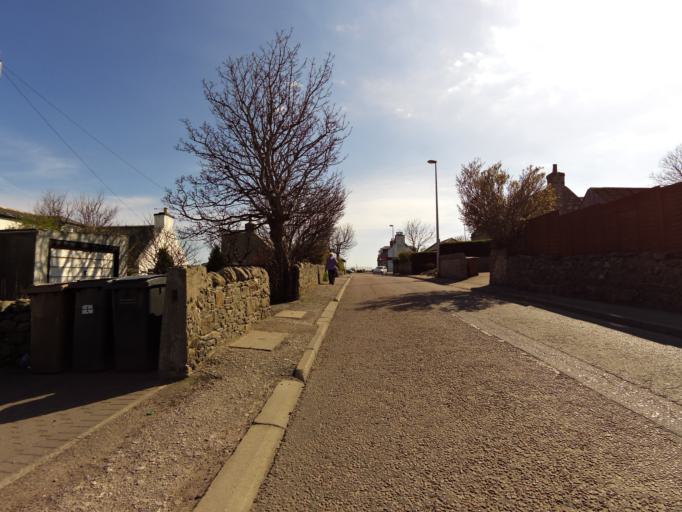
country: GB
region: Scotland
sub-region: Aberdeen City
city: Aberdeen
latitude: 57.0995
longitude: -2.0799
